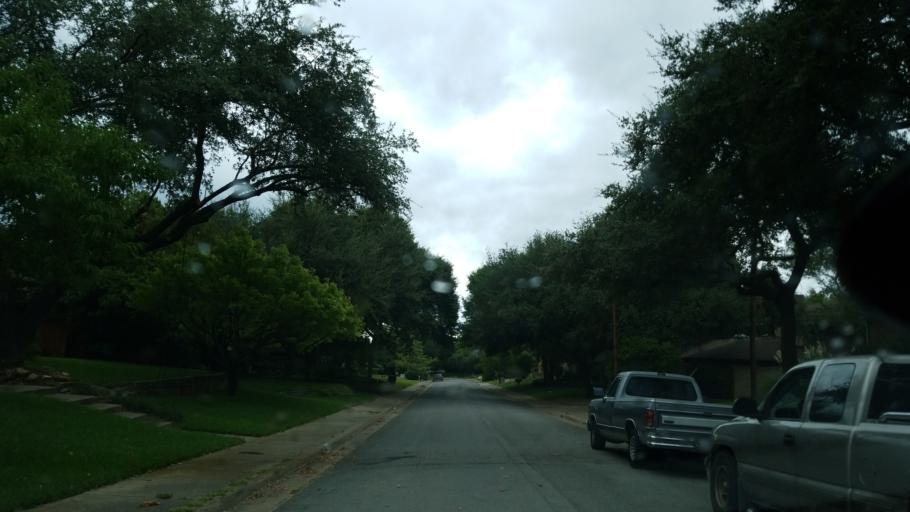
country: US
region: Texas
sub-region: Dallas County
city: Richardson
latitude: 32.8958
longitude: -96.7362
